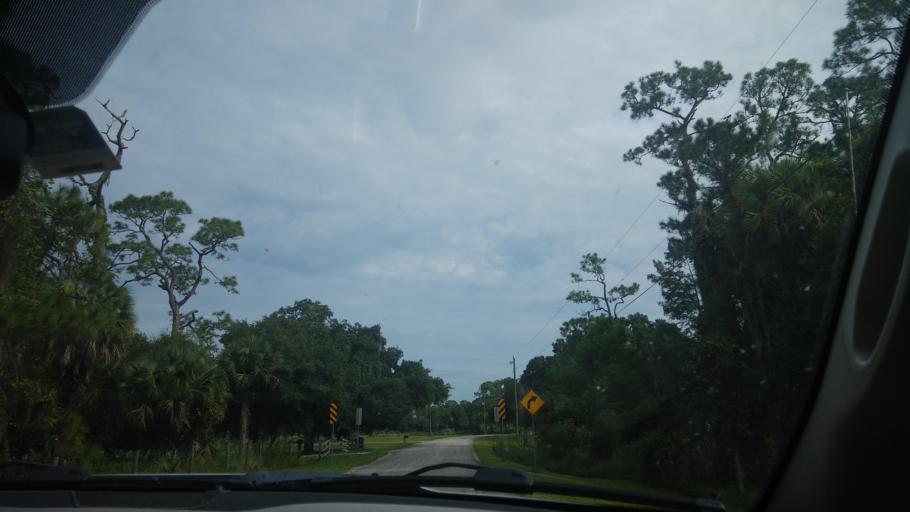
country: US
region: Florida
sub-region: Indian River County
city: Fellsmere
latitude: 27.6862
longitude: -80.7974
